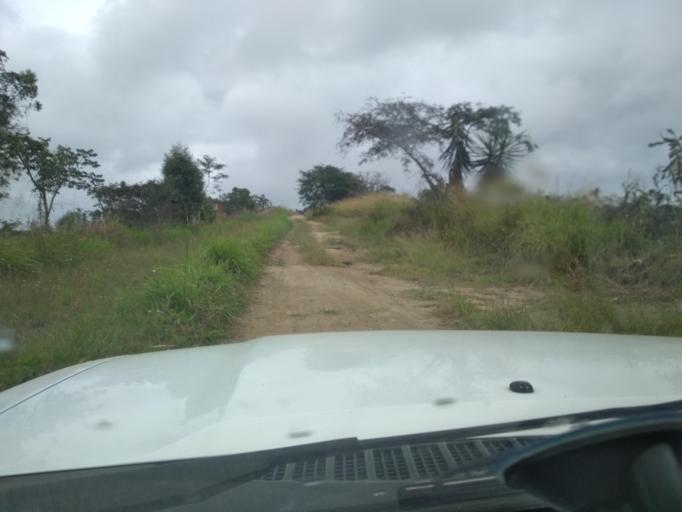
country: MX
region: Veracruz
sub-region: Emiliano Zapata
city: Dos Rios
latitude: 19.5325
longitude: -96.8101
